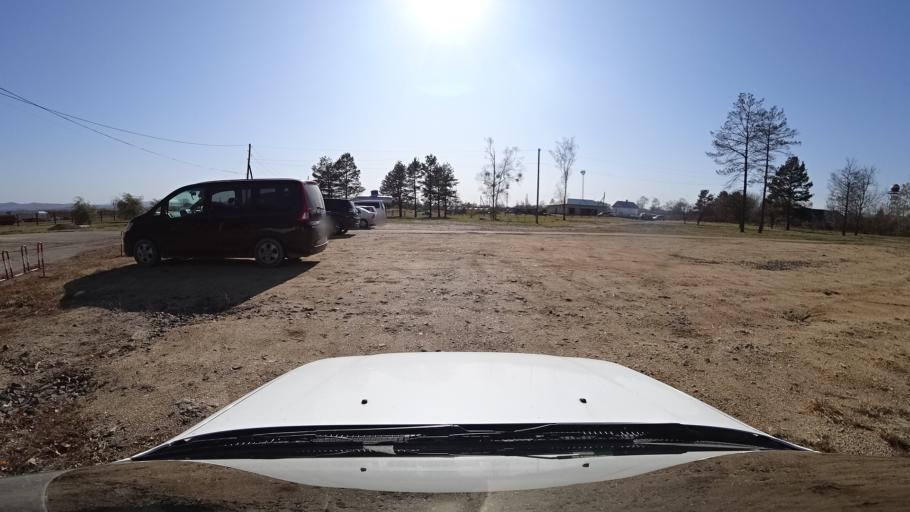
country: RU
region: Primorskiy
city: Dal'nerechensk
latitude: 45.8799
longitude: 133.7303
